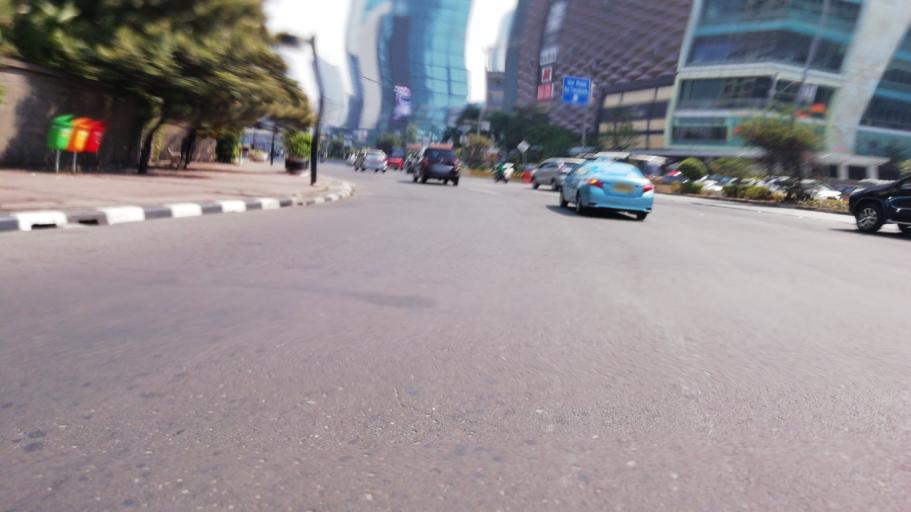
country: ID
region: Jakarta Raya
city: Jakarta
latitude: -6.1956
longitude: 106.8232
